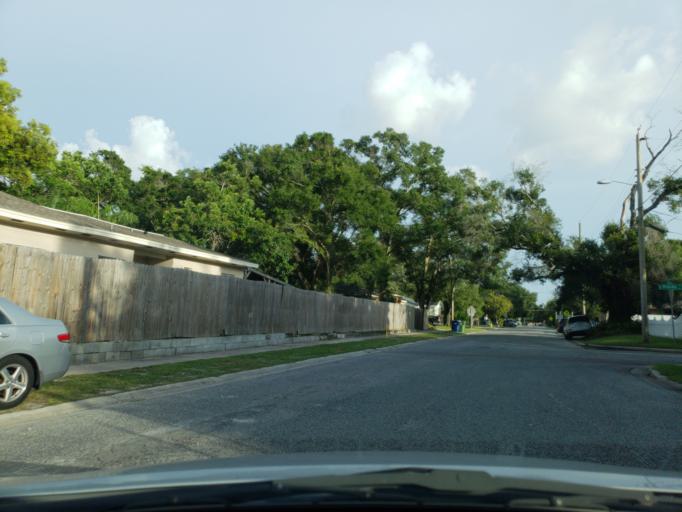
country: US
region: Florida
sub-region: Hillsborough County
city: Tampa
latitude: 27.9777
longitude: -82.4409
